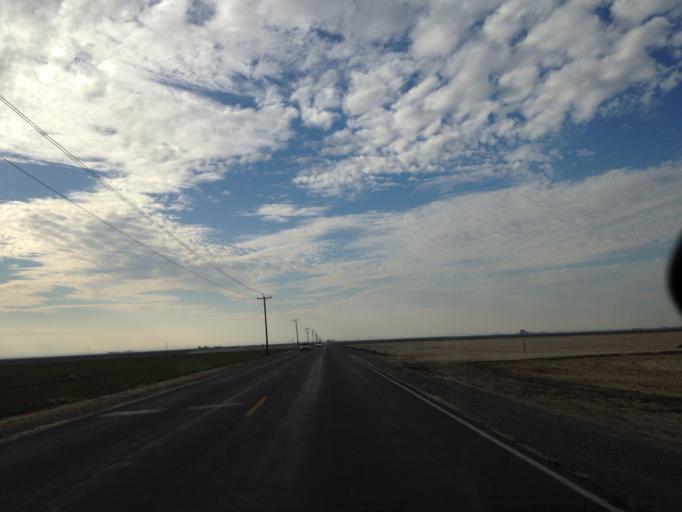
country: US
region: California
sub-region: Kern County
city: Buttonwillow
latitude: 35.4424
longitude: -119.4875
